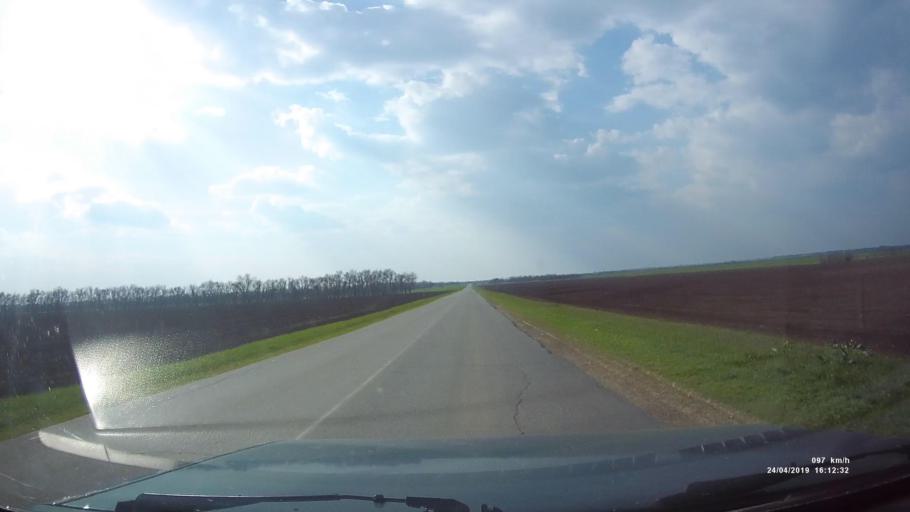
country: RU
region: Rostov
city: Sovetskoye
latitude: 46.7336
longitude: 42.2358
